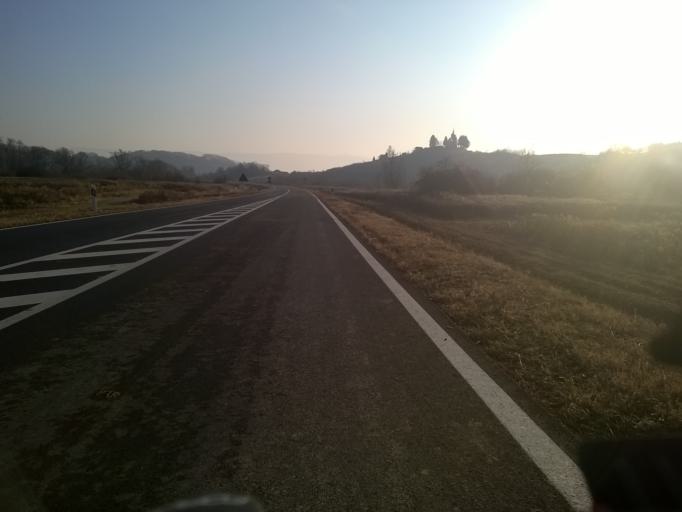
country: HR
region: Krapinsko-Zagorska
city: Zabok
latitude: 46.0444
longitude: 15.9144
